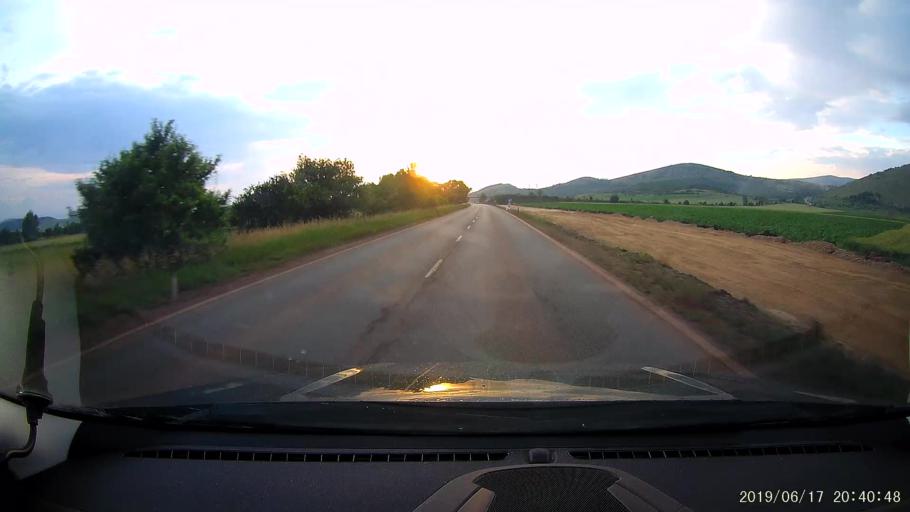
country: BG
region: Sofiya
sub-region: Obshtina Dragoman
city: Dragoman
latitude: 42.8902
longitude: 22.9800
